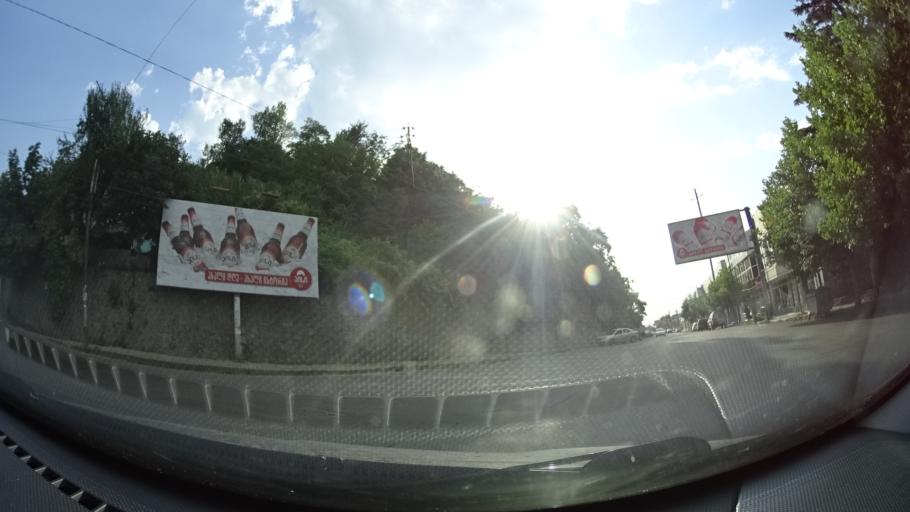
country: GE
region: Kakheti
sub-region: Telavi
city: Telavi
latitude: 41.9213
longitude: 45.4739
